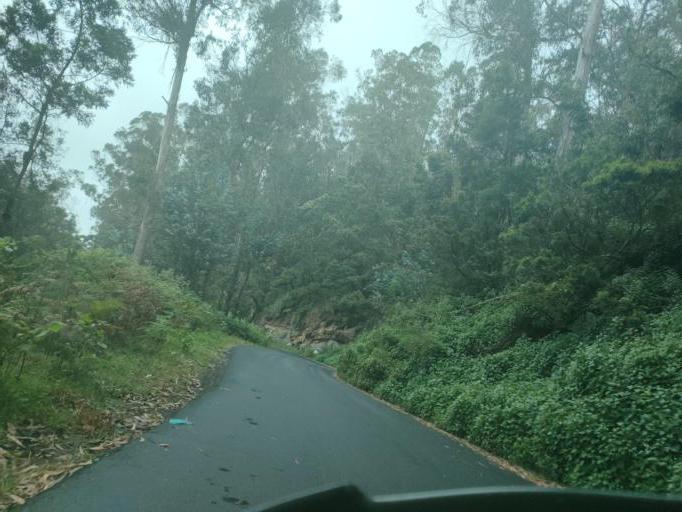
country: IN
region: Tamil Nadu
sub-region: Dindigul
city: Kodaikanal
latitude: 10.2432
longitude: 77.3616
